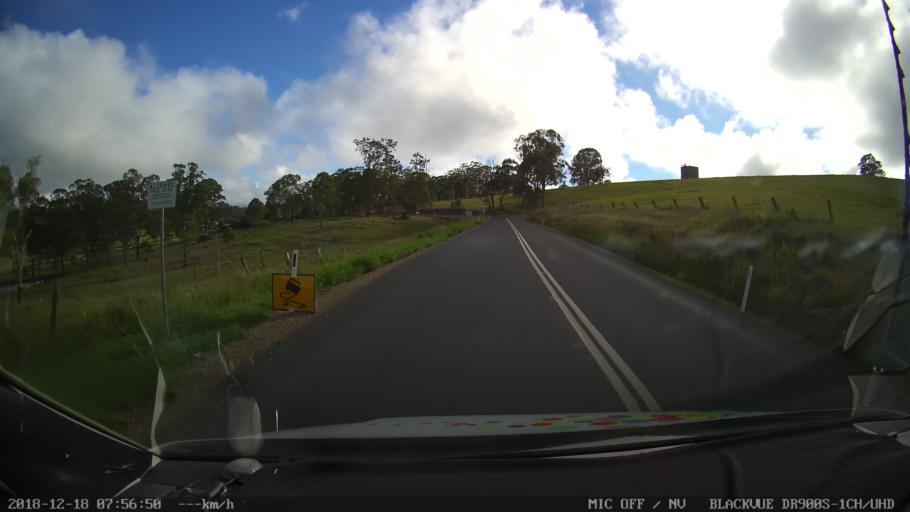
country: AU
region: New South Wales
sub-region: Kyogle
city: Kyogle
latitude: -28.3969
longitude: 152.6090
